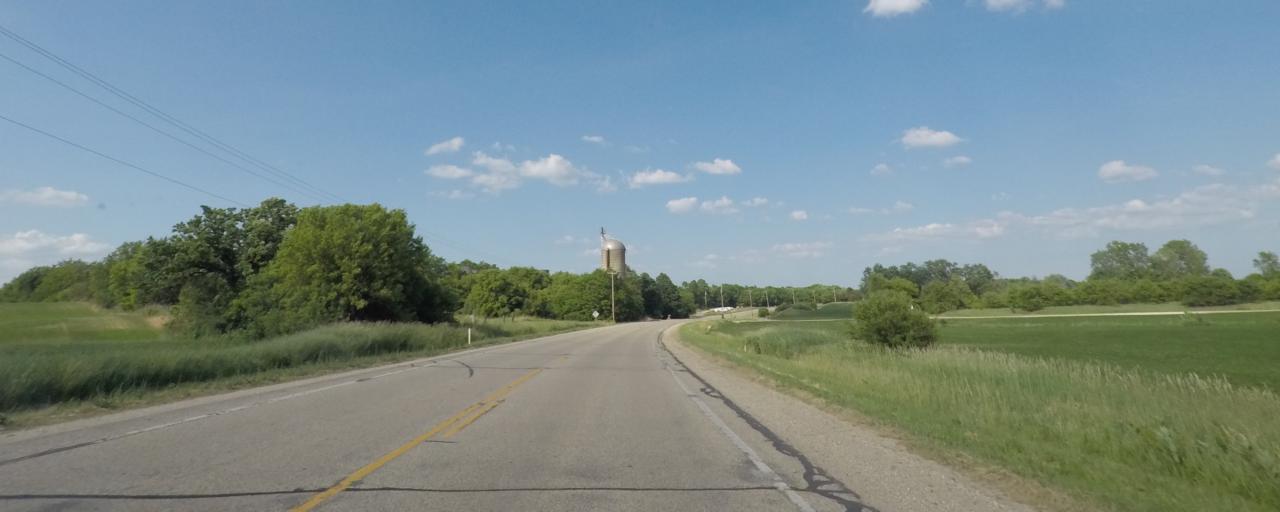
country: US
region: Wisconsin
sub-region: Walworth County
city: Potter Lake
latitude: 42.8258
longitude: -88.3168
